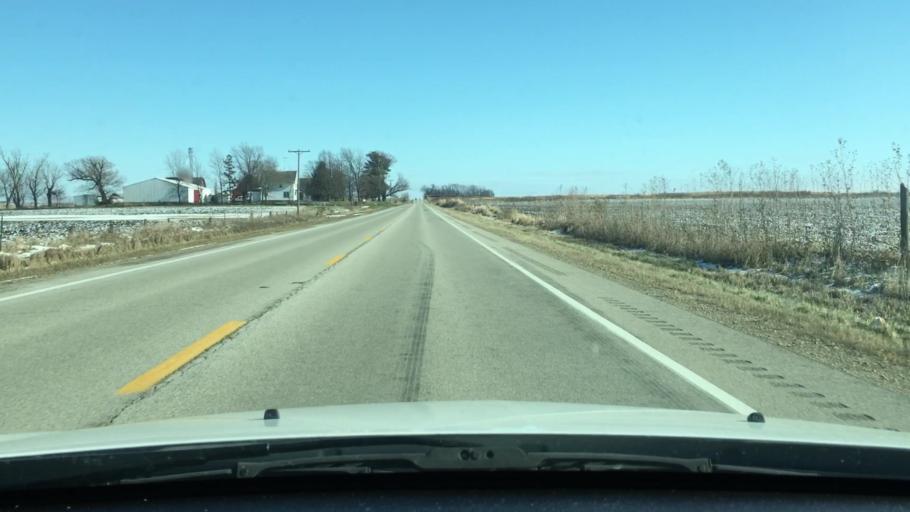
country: US
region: Illinois
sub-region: DeKalb County
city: Malta
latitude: 42.0008
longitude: -88.9136
